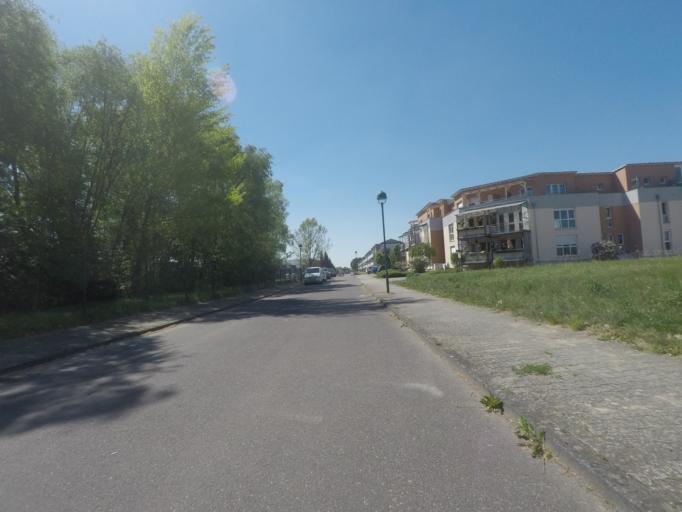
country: DE
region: Brandenburg
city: Melchow
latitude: 52.8507
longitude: 13.6964
